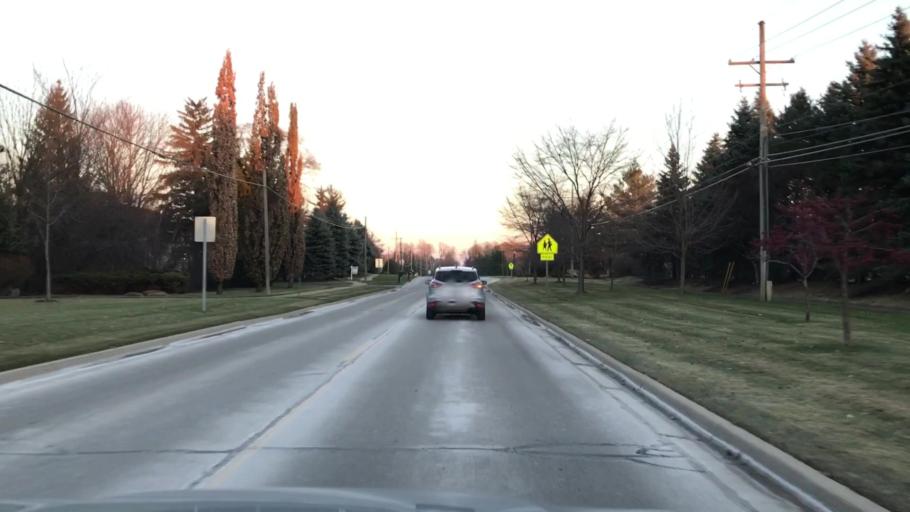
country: US
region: Michigan
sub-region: Wayne County
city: Northville
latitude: 42.4511
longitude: -83.5078
